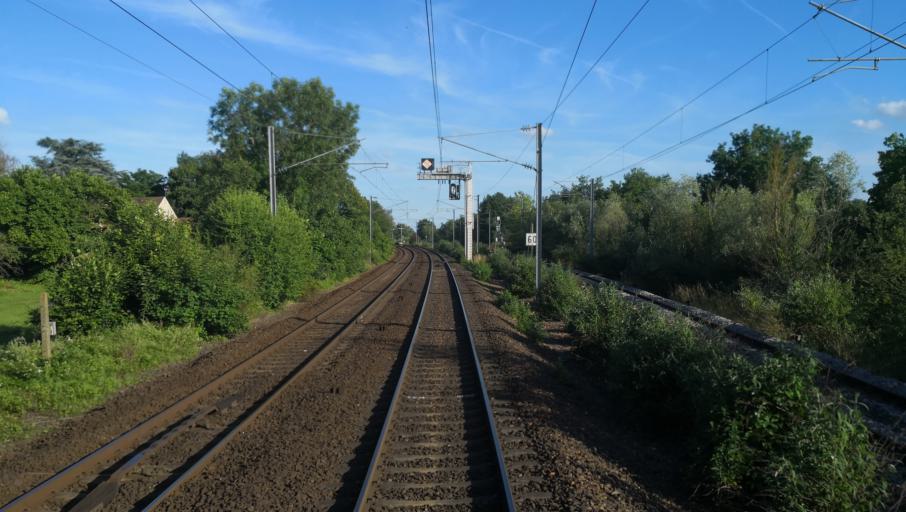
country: FR
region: Haute-Normandie
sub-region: Departement de l'Eure
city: Bueil
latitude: 48.9287
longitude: 1.4400
